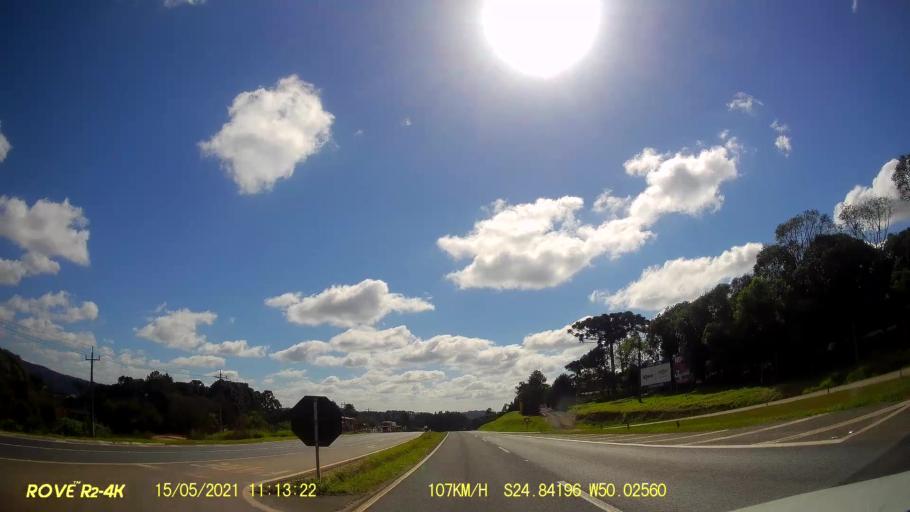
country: BR
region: Parana
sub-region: Castro
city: Castro
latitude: -24.8421
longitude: -50.0256
